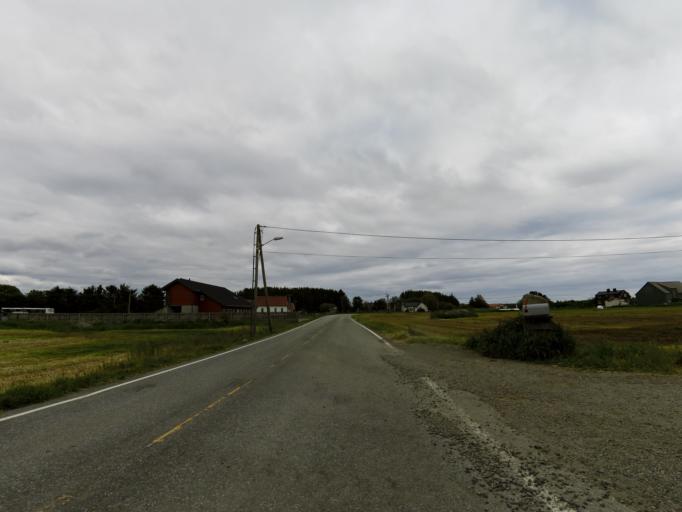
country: NO
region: Vest-Agder
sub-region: Farsund
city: Vestbygd
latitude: 58.1171
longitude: 6.6031
